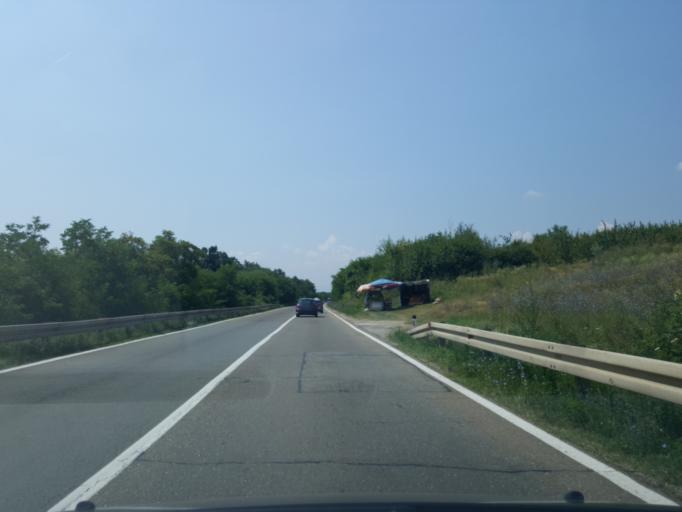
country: RS
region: Central Serbia
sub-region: Belgrade
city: Sopot
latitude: 44.5288
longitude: 20.6557
